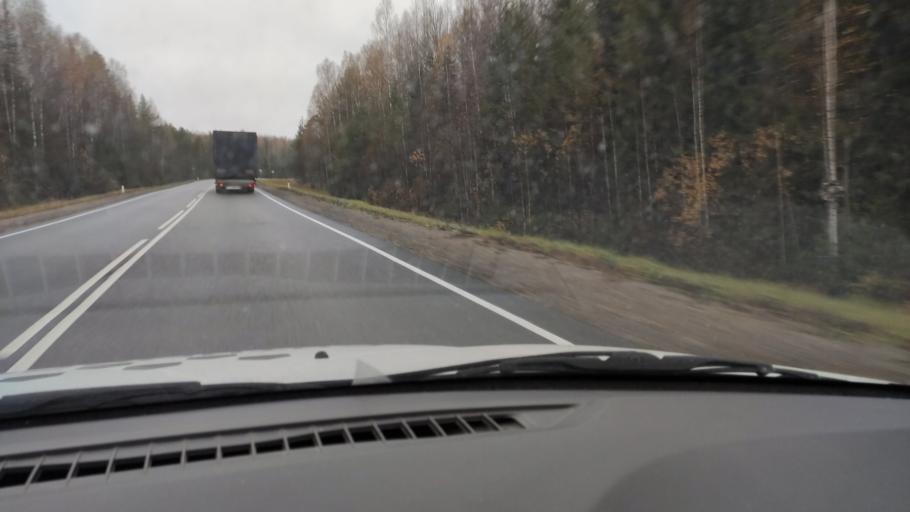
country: RU
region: Kirov
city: Chernaya Kholunitsa
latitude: 58.8294
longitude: 51.7663
